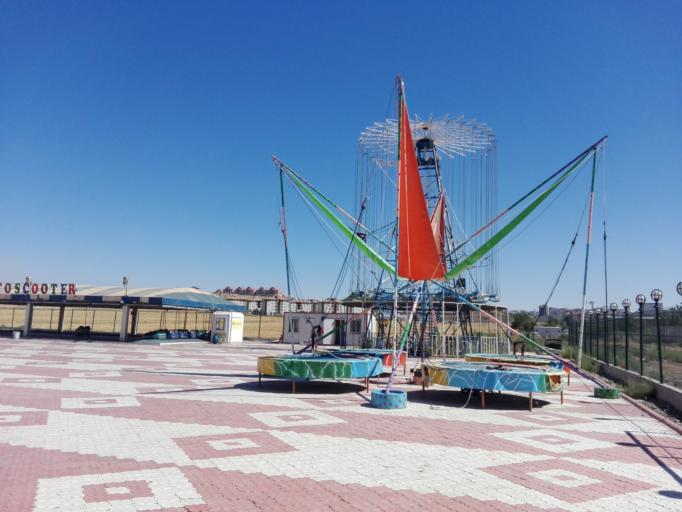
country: TR
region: Batman
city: Batman
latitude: 37.9079
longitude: 41.1191
